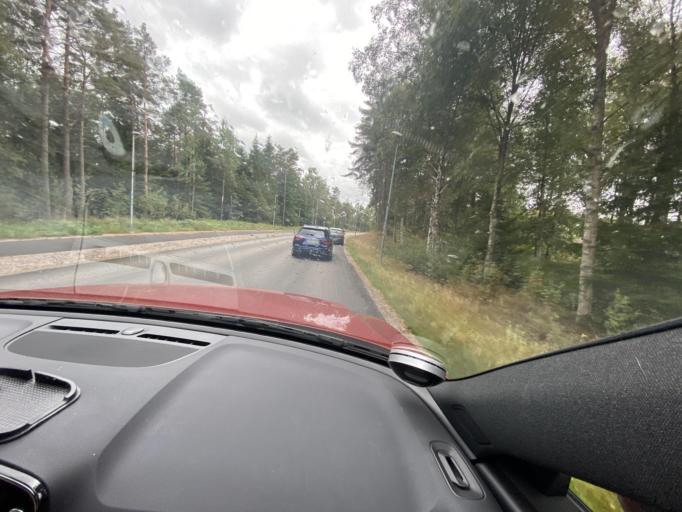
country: SE
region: Kronoberg
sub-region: Markaryds Kommun
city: Markaryd
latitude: 56.4550
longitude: 13.6178
